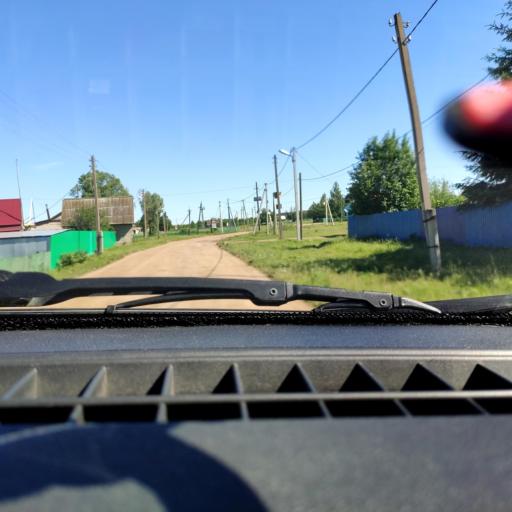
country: RU
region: Bashkortostan
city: Iglino
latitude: 54.8941
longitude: 56.4967
